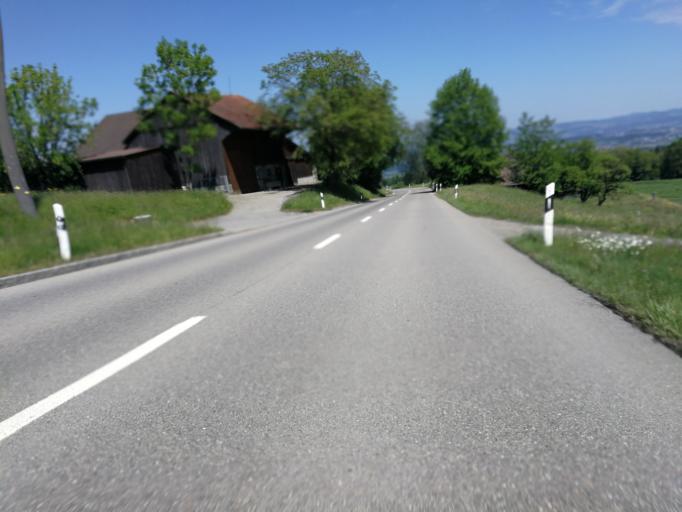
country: CH
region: Zurich
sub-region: Bezirk Uster
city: Esslingen
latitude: 47.2779
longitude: 8.6972
